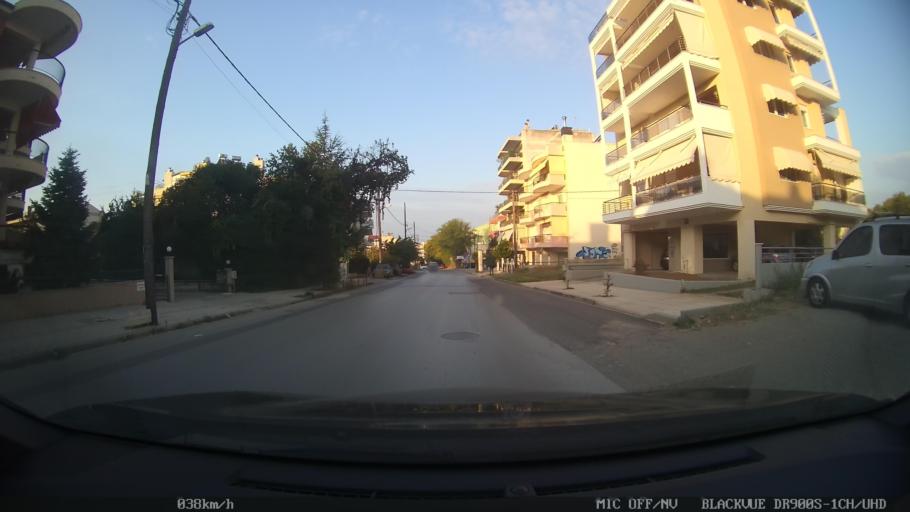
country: GR
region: Central Macedonia
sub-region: Nomos Thessalonikis
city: Pylaia
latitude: 40.5961
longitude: 22.9768
